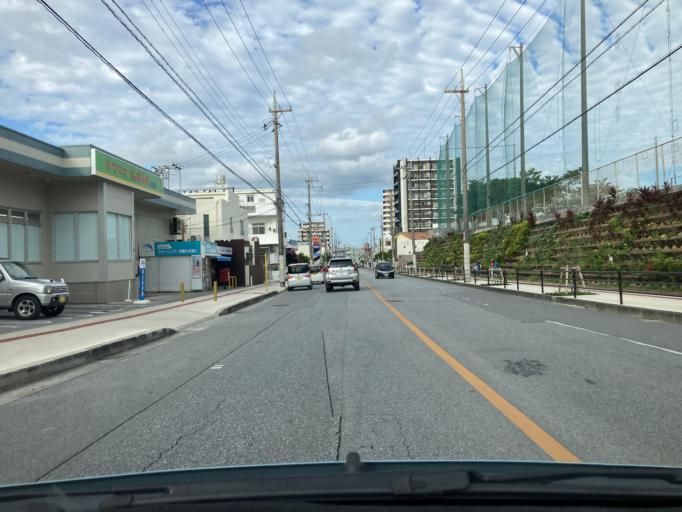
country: JP
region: Okinawa
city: Okinawa
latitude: 26.3388
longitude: 127.8213
